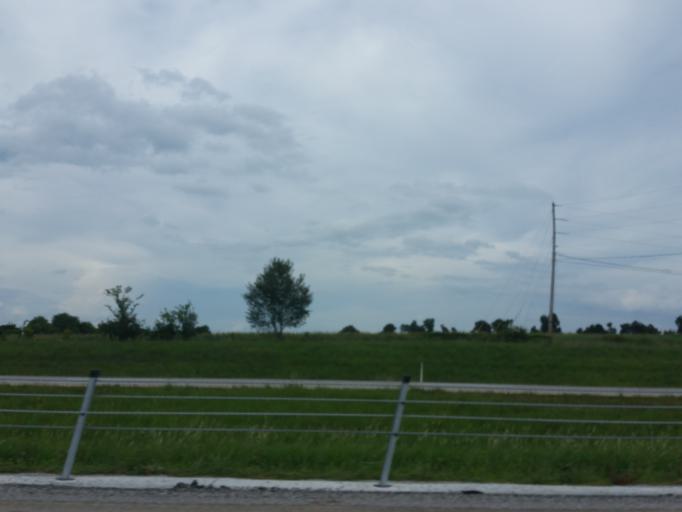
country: US
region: Kentucky
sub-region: Trigg County
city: Cadiz
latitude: 36.9682
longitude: -87.8791
